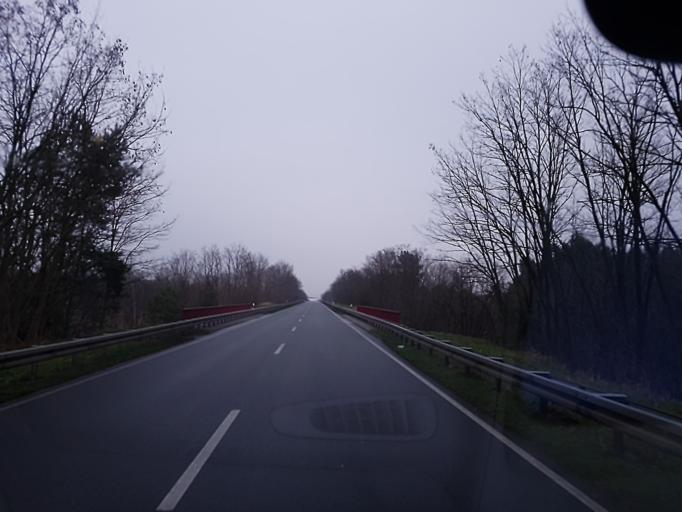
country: DE
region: Brandenburg
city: Lubbenau
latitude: 51.8380
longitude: 13.9382
